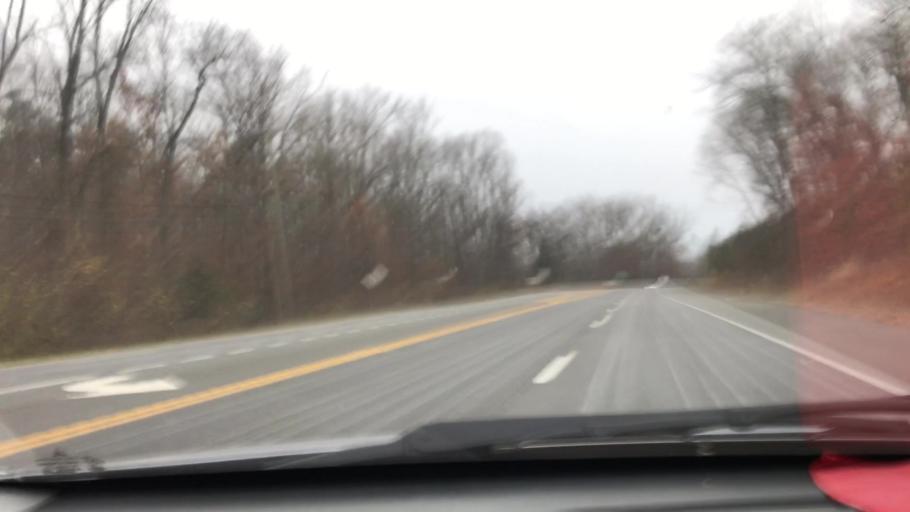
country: US
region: Virginia
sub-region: Prince William County
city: Triangle
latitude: 38.5424
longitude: -77.3389
